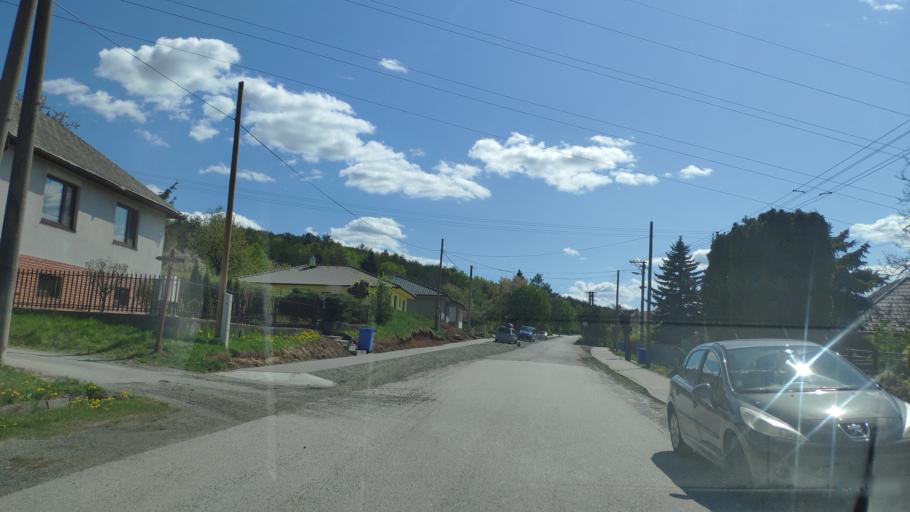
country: SK
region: Kosicky
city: Kosice
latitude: 48.6769
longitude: 21.4308
